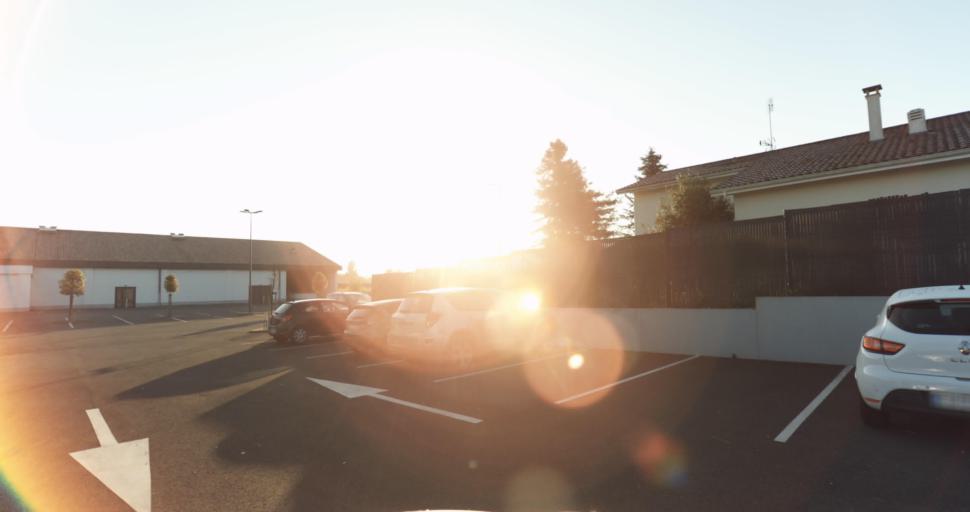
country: FR
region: Aquitaine
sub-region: Departement de la Gironde
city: Bazas
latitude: 44.4384
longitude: -0.2272
